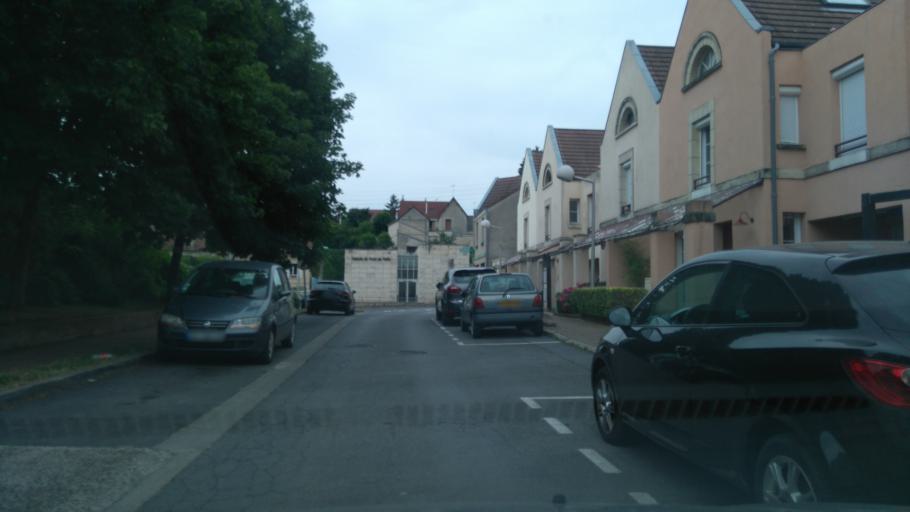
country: FR
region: Picardie
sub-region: Departement de l'Oise
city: Saint-Maximin
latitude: 49.2218
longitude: 2.4438
